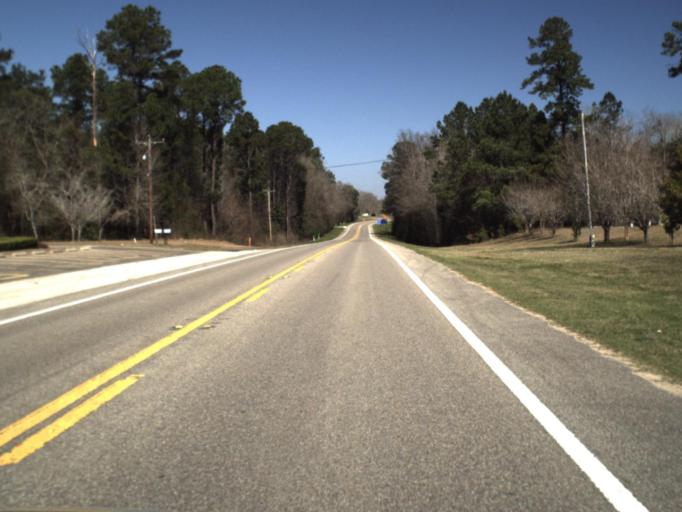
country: US
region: Florida
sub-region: Calhoun County
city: Blountstown
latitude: 30.4784
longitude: -85.0457
